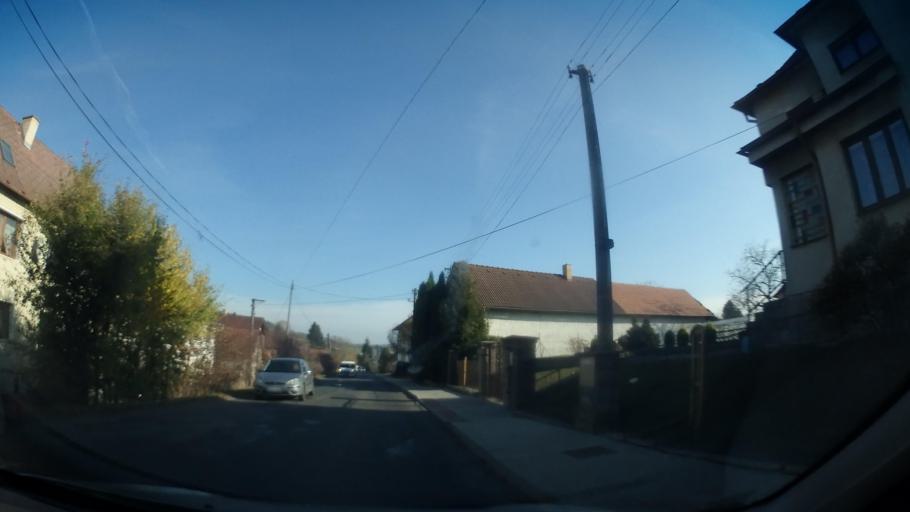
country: CZ
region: Central Bohemia
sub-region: Okres Praha-Vychod
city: Strancice
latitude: 49.9601
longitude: 14.6797
